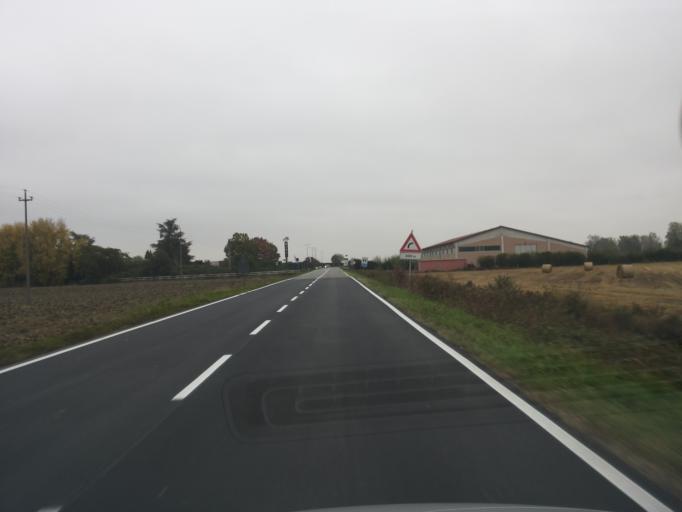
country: IT
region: Piedmont
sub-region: Provincia di Novara
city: Casalino
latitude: 45.3923
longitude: 8.5090
